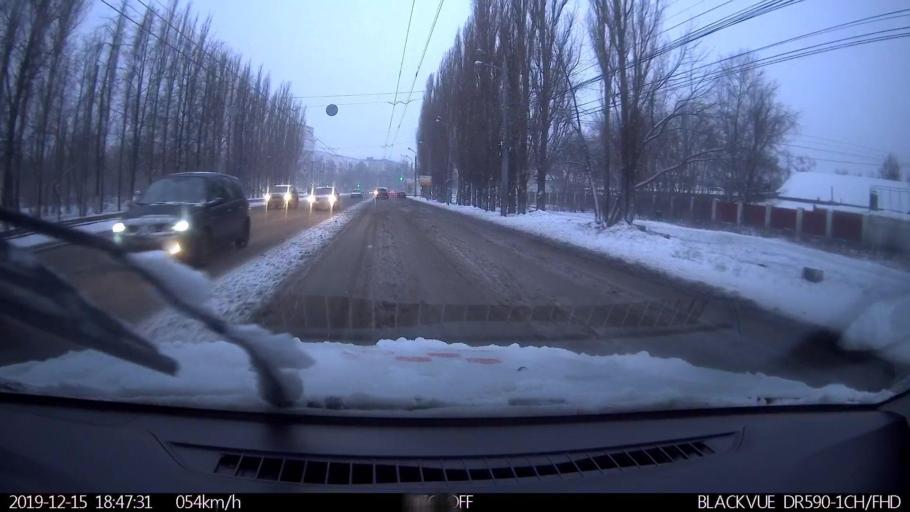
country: RU
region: Nizjnij Novgorod
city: Nizhniy Novgorod
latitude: 56.3354
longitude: 43.8888
